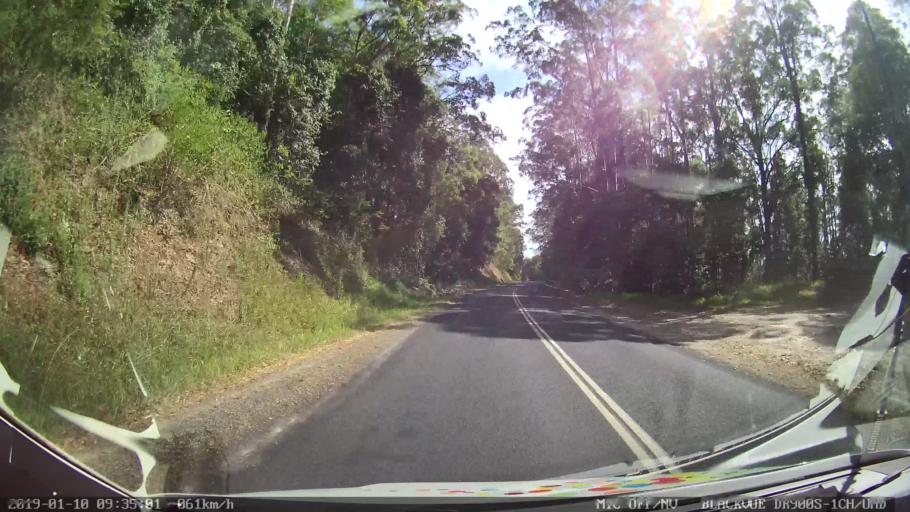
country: AU
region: New South Wales
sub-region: Coffs Harbour
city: Nana Glen
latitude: -30.2148
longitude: 153.0095
